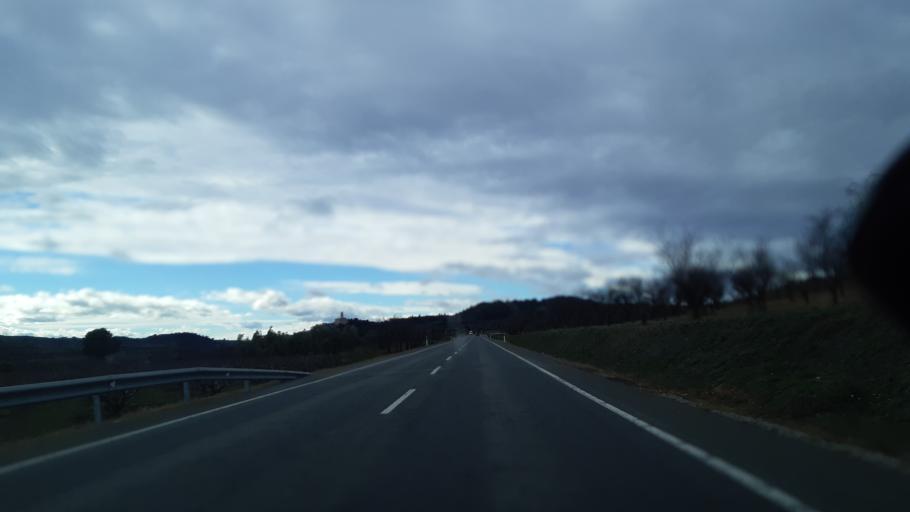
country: ES
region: Catalonia
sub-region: Provincia de Tarragona
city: Gandesa
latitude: 41.0856
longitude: 0.5021
